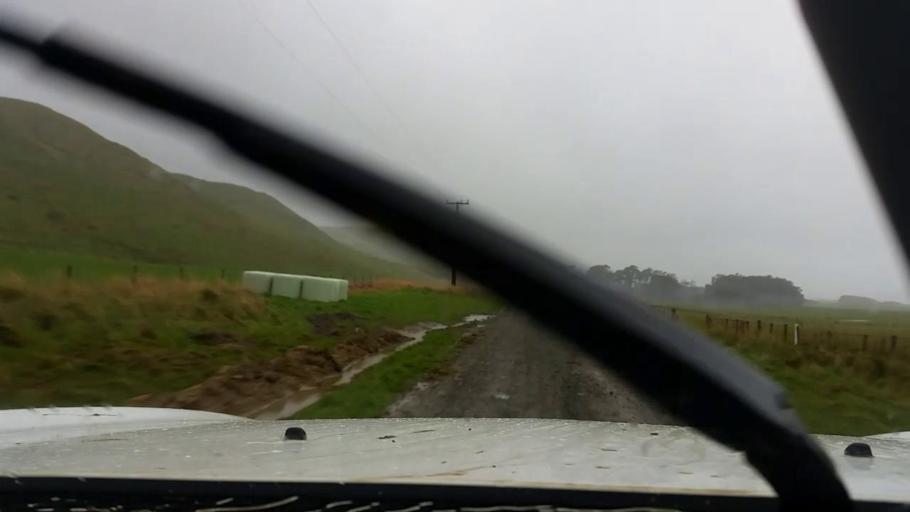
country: NZ
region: Wellington
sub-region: Masterton District
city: Masterton
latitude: -41.2557
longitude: 175.9073
